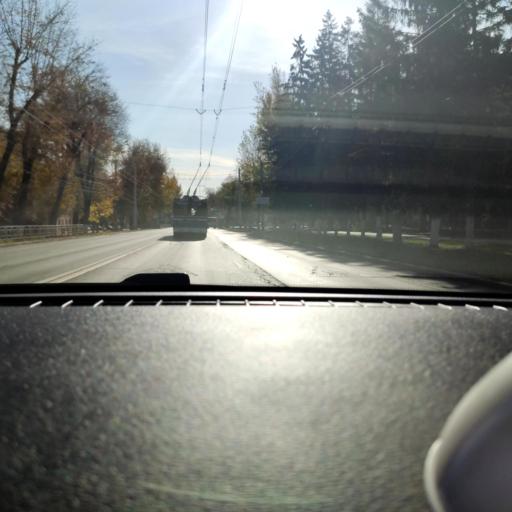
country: RU
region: Samara
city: Samara
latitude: 53.2290
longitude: 50.2504
